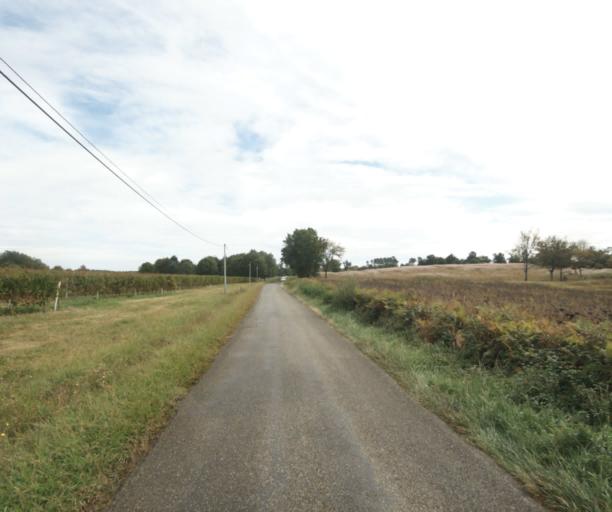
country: FR
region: Midi-Pyrenees
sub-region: Departement du Gers
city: Cazaubon
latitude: 43.9022
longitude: -0.1297
